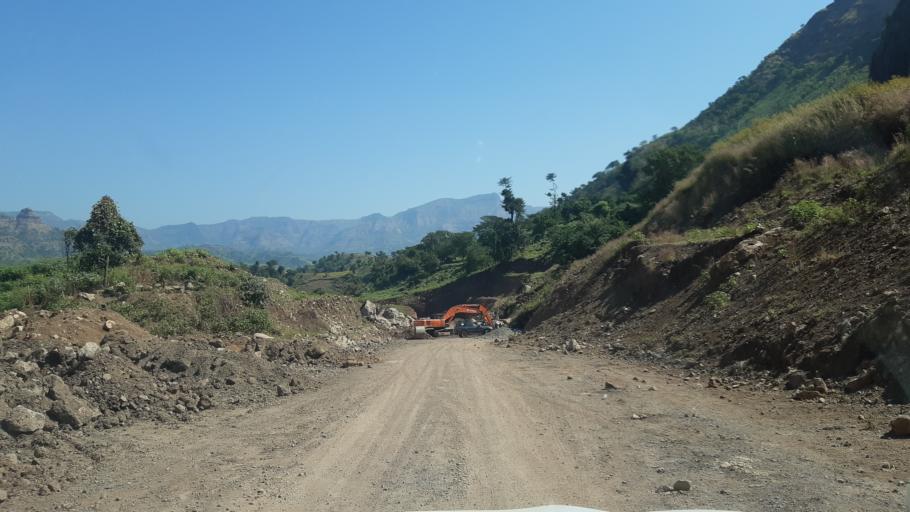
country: ET
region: Amhara
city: Dabat
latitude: 13.1820
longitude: 37.5969
